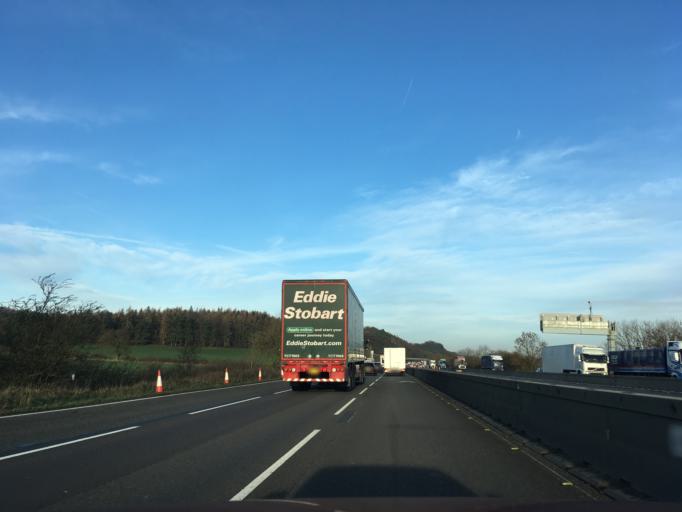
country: GB
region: England
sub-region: Staffordshire
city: Barlaston
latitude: 52.9291
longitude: -2.2106
